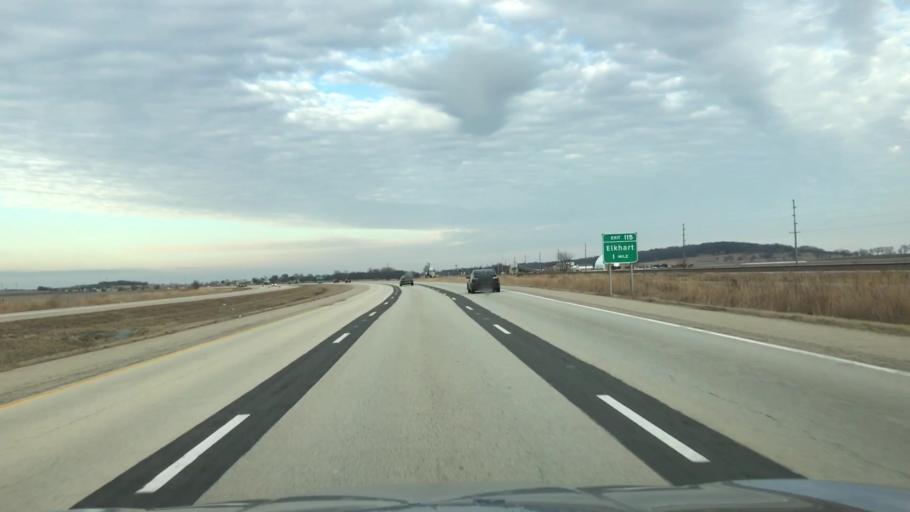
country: US
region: Illinois
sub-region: Sangamon County
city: Williamsville
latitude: 40.0005
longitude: -89.5046
